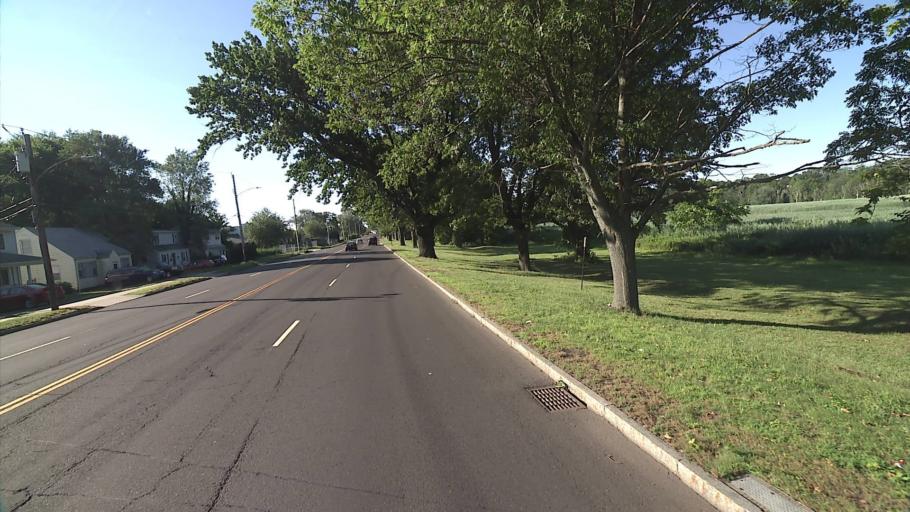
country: US
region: Connecticut
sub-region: New Haven County
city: New Haven
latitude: 41.3044
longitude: -72.9523
